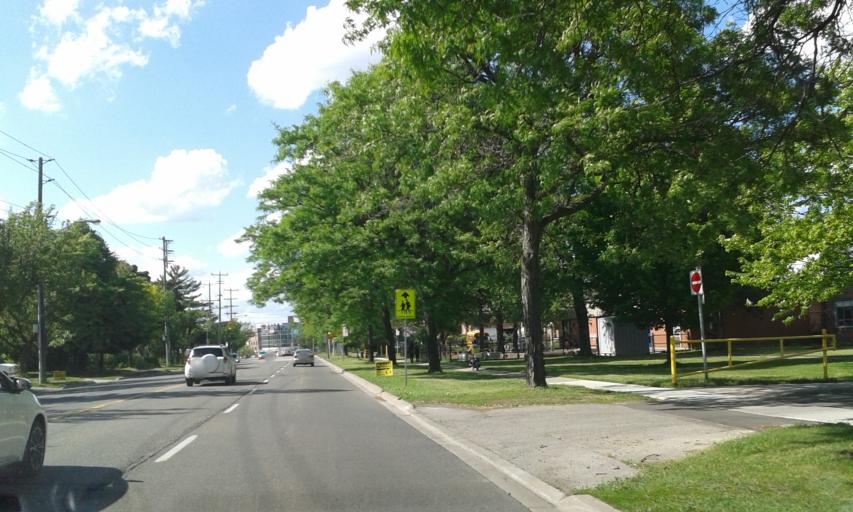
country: CA
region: Ontario
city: Scarborough
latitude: 43.7842
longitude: -79.2666
